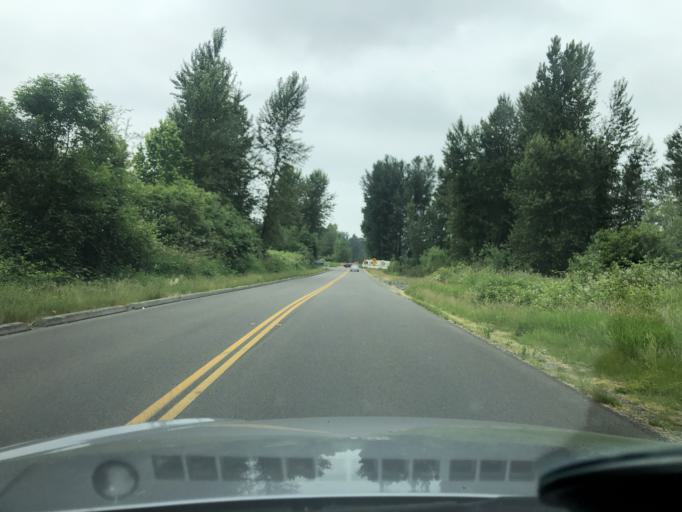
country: US
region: Washington
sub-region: King County
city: Kent
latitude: 47.3468
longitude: -122.2193
